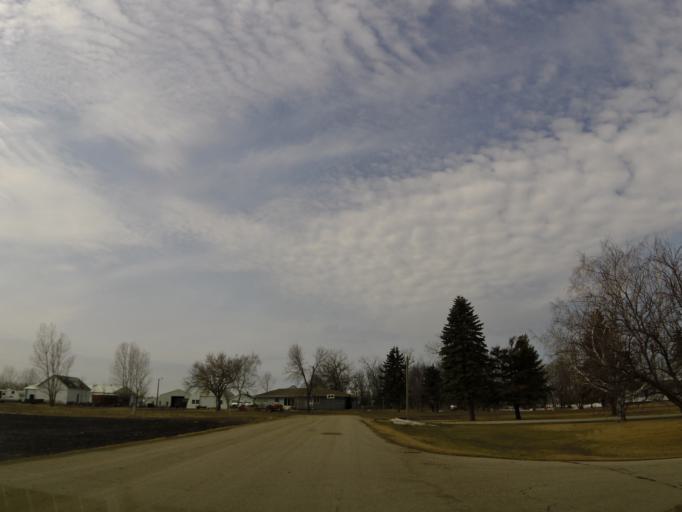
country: US
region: North Dakota
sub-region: Walsh County
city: Grafton
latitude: 48.2915
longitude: -97.3823
